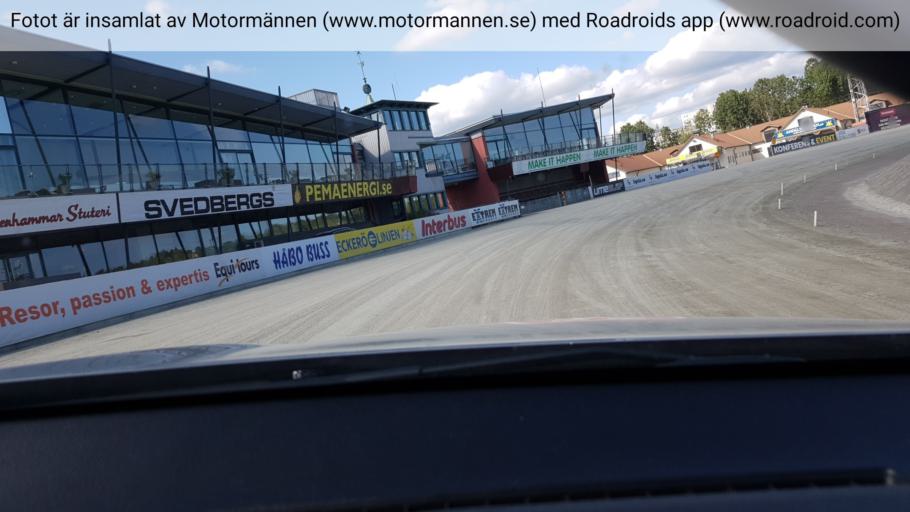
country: SE
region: Stockholm
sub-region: Stockholms Kommun
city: Bromma
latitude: 59.3678
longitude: 17.9369
